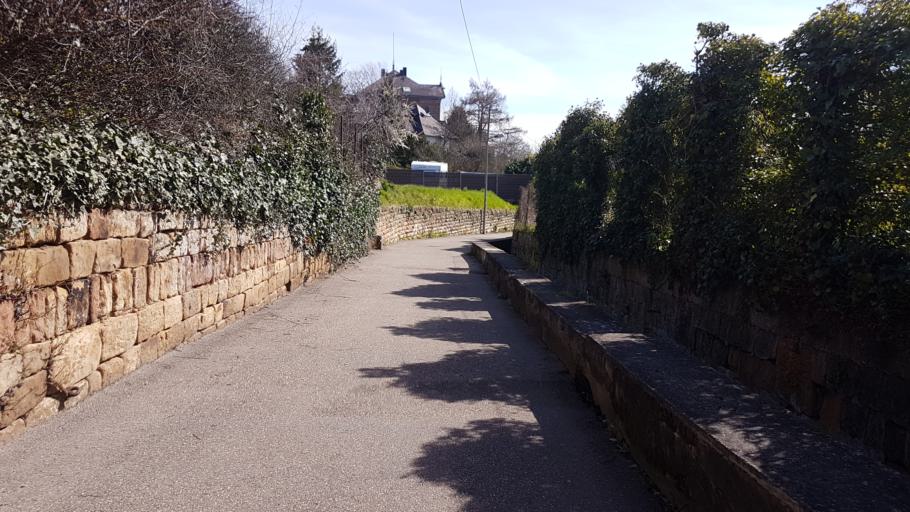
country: DE
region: Rheinland-Pfalz
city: Neustadt
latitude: 49.3598
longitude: 8.1392
